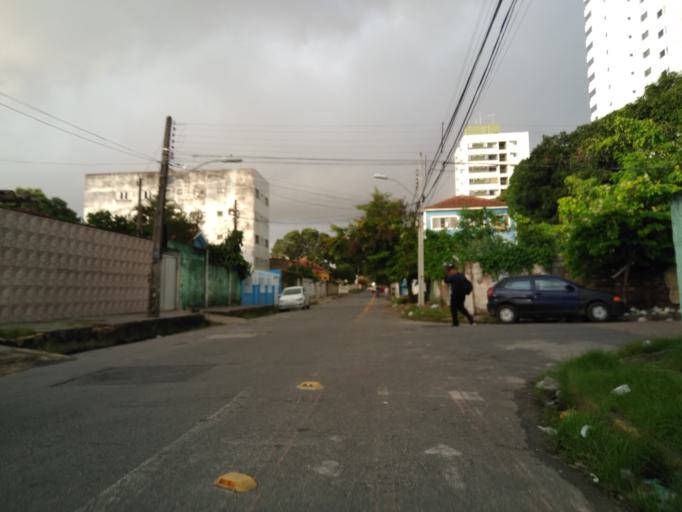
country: BR
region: Pernambuco
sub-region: Recife
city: Recife
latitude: -8.0359
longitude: -34.8909
